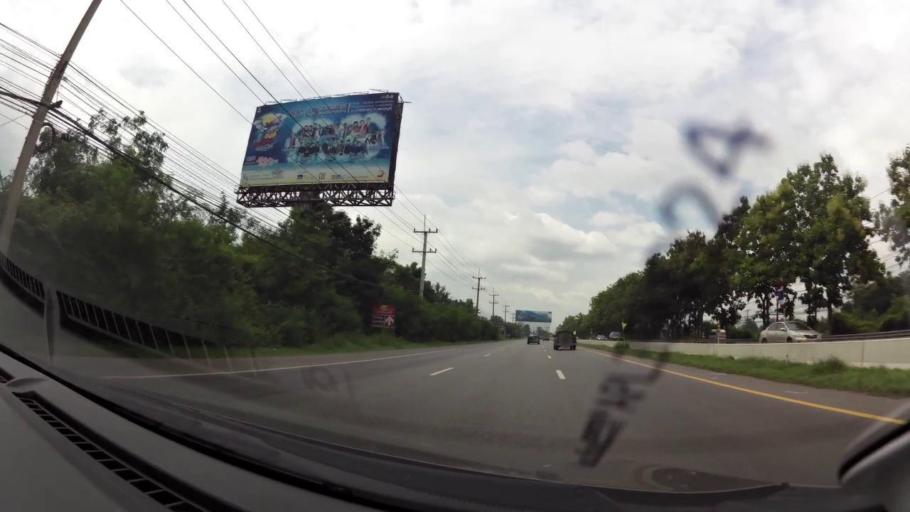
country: TH
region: Phetchaburi
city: Khao Yoi
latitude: 13.2553
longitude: 99.8248
